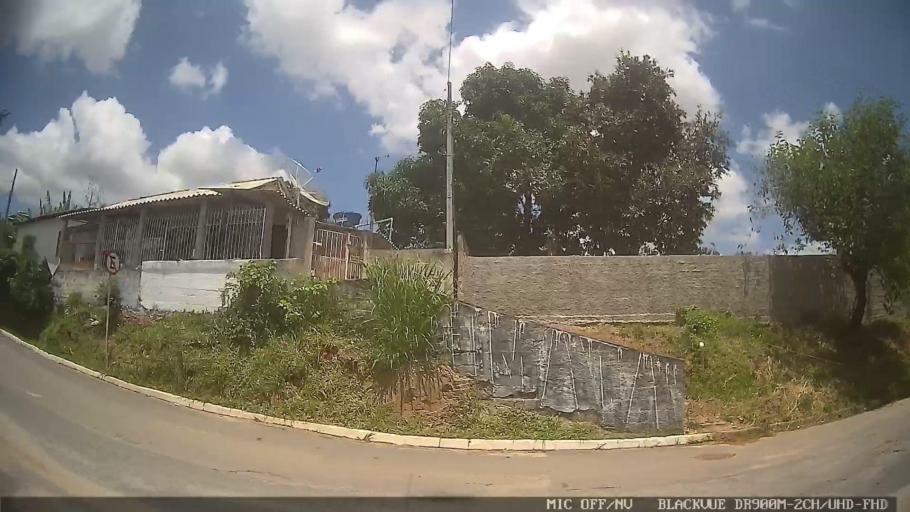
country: BR
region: Sao Paulo
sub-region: Jacarei
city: Jacarei
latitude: -23.3000
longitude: -45.9493
